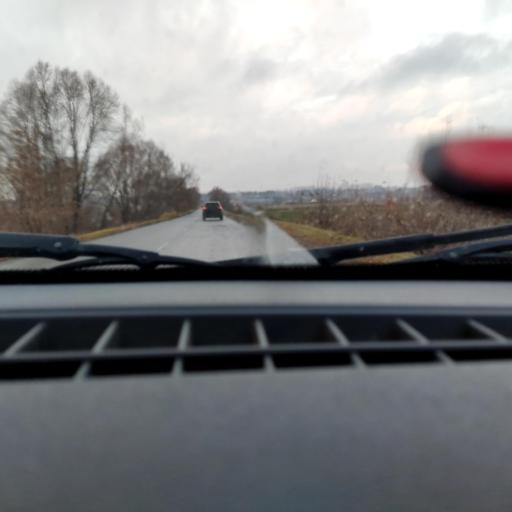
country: RU
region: Bashkortostan
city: Avdon
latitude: 54.5046
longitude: 55.8780
